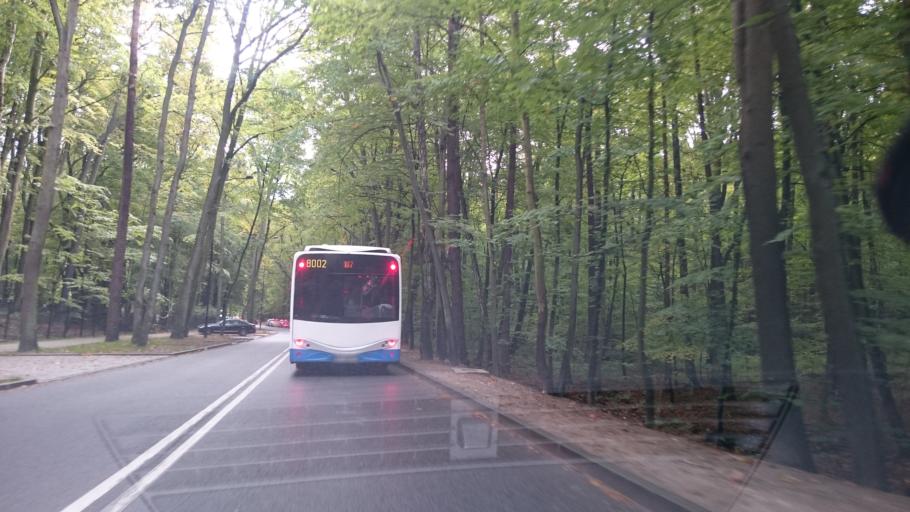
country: PL
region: Pomeranian Voivodeship
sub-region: Sopot
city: Sopot
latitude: 54.4519
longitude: 18.5424
